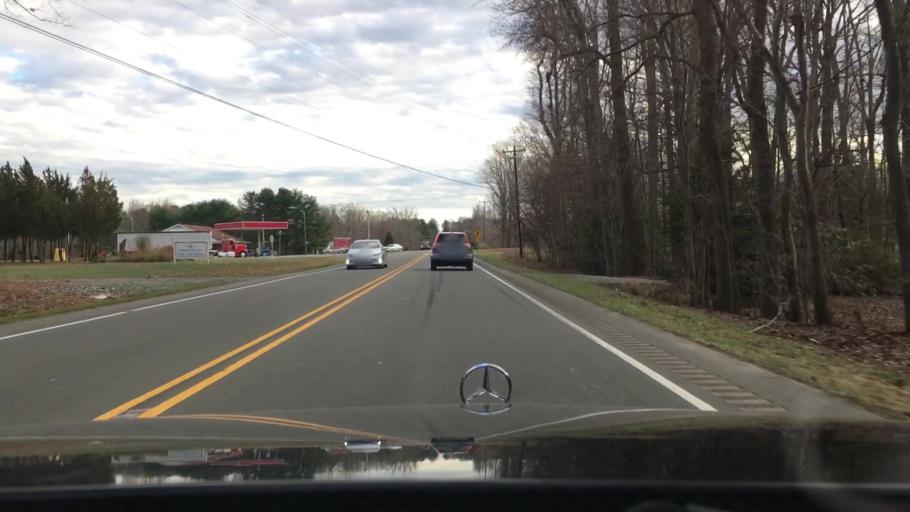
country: US
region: North Carolina
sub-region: Orange County
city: Hillsborough
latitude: 36.1377
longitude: -79.1208
